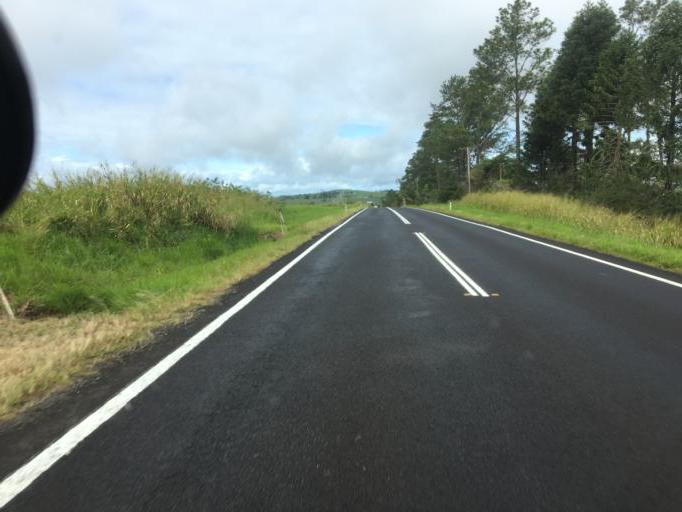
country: AU
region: Queensland
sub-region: Tablelands
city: Ravenshoe
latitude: -17.5200
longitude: 145.6419
